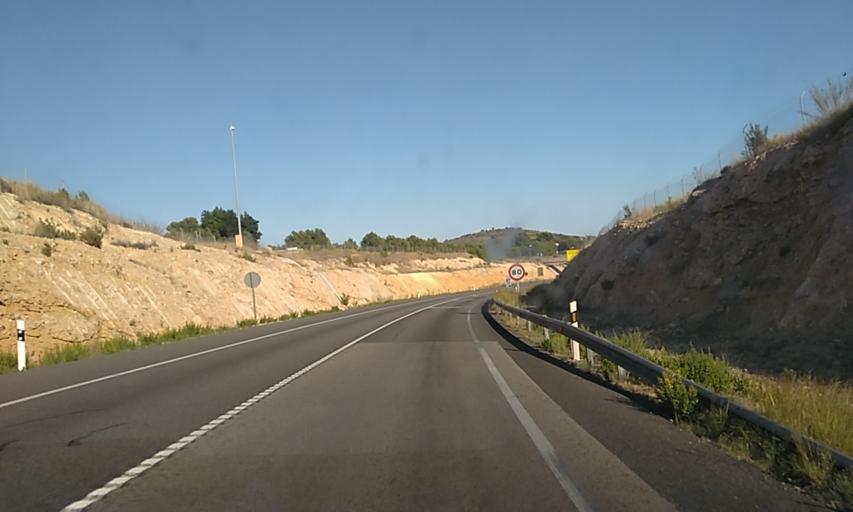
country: ES
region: Valencia
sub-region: Provincia de Castello
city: Torreblanca
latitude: 40.2323
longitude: 0.2062
